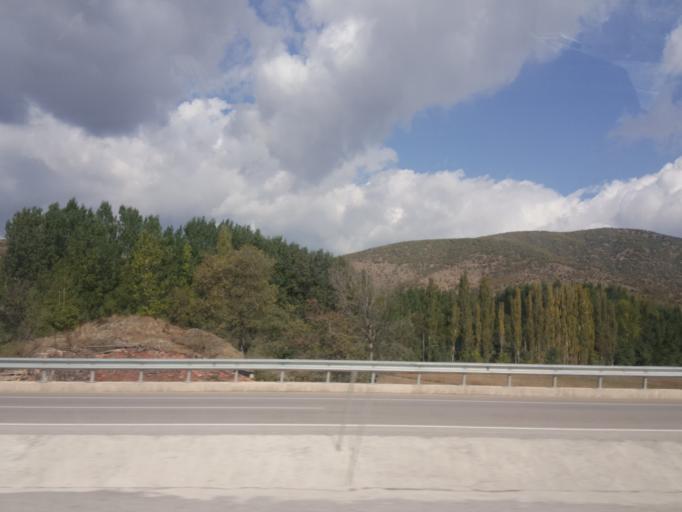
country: TR
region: Tokat
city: Gokdere
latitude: 40.3799
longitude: 36.6830
